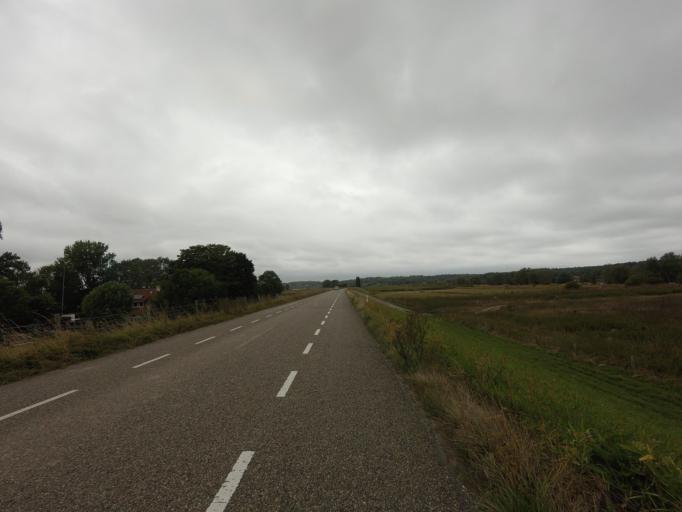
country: NL
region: Gelderland
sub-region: Gemeente Renkum
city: Oosterbeek
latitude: 51.9696
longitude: 5.8467
